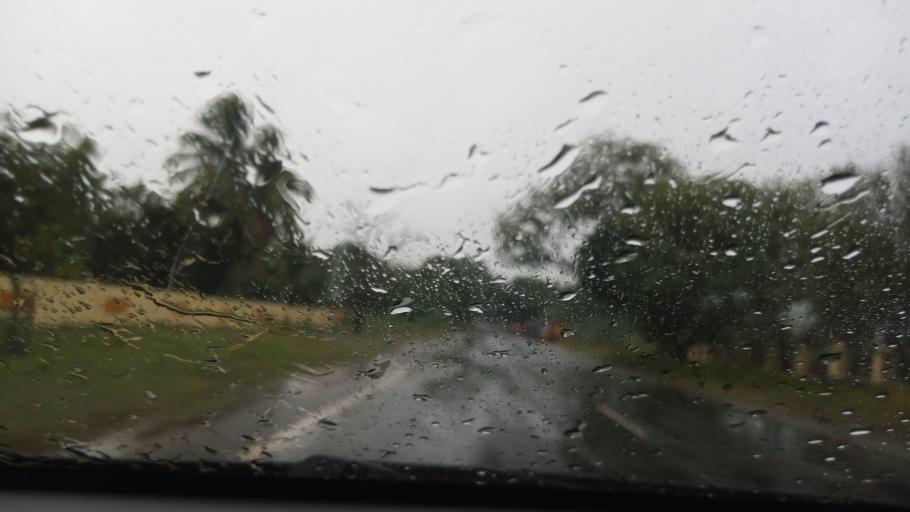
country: IN
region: Tamil Nadu
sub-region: Vellore
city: Kalavai
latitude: 12.8032
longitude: 79.4309
